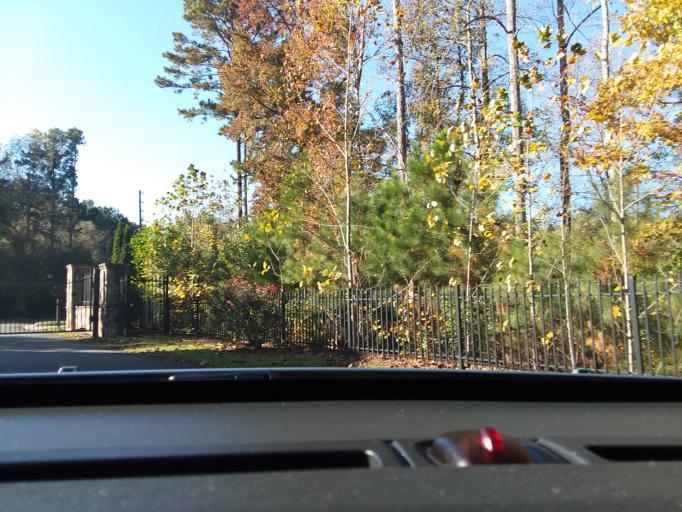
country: US
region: Georgia
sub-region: Fulton County
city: Johns Creek
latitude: 34.0021
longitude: -84.2672
